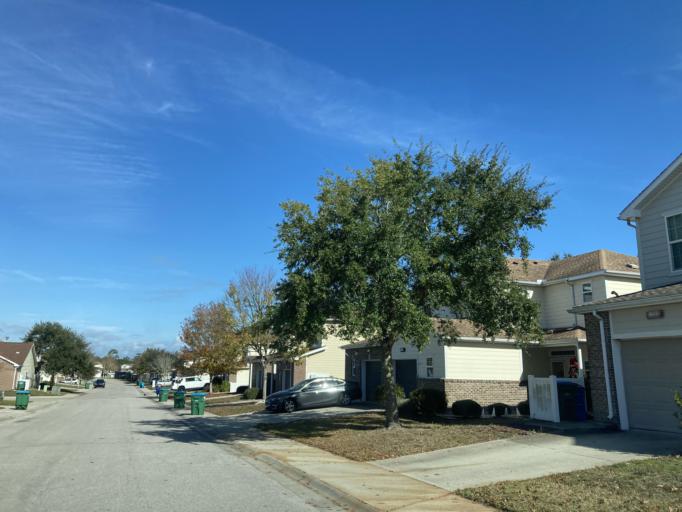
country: US
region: Mississippi
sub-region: Harrison County
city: D'Iberville
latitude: 30.4052
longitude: -88.9481
